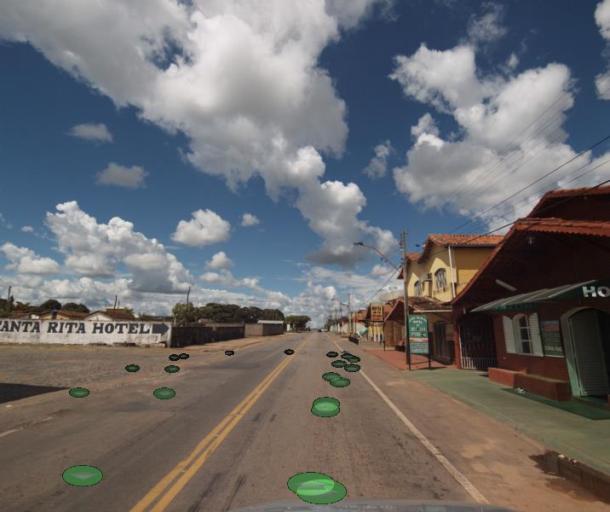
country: BR
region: Goias
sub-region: Porangatu
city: Porangatu
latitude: -13.7143
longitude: -49.0204
